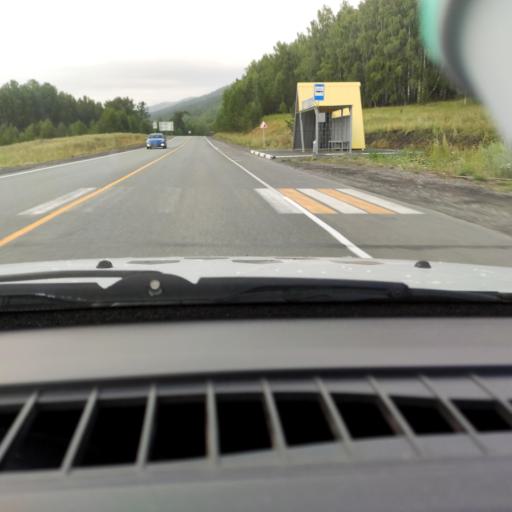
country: RU
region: Chelyabinsk
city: Turgoyak
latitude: 55.2399
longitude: 60.1926
